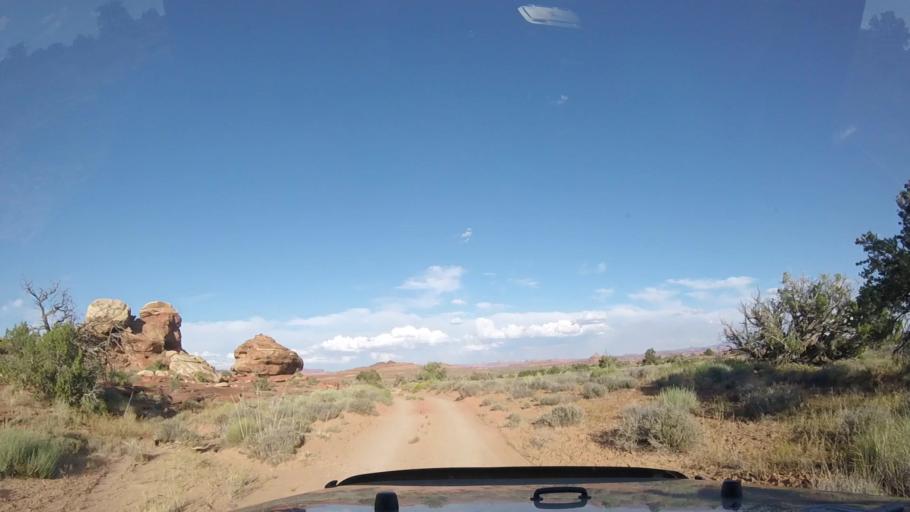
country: US
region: Utah
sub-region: Grand County
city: Moab
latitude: 38.2123
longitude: -109.8075
